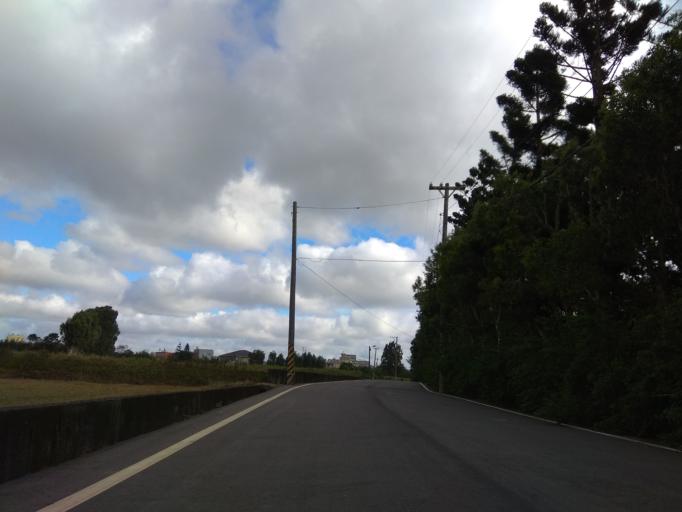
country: TW
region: Taiwan
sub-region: Hsinchu
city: Zhubei
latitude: 24.9740
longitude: 121.0845
